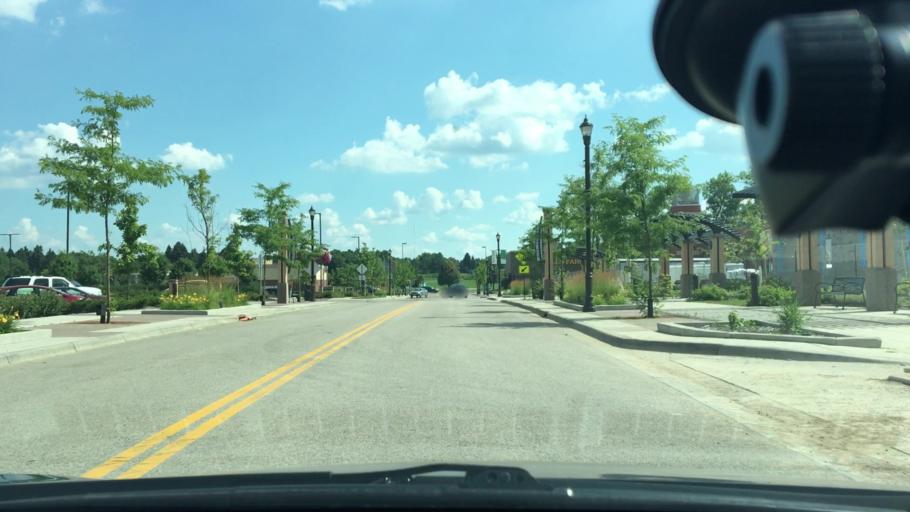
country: US
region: Minnesota
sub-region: Hennepin County
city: New Hope
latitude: 45.0350
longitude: -93.3854
